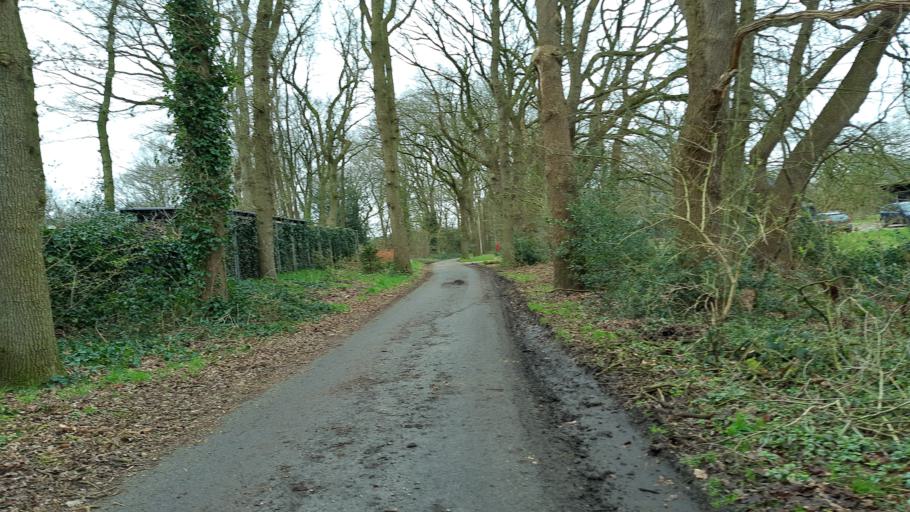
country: NL
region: Drenthe
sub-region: Gemeente Assen
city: Assen
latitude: 52.8498
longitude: 6.5965
